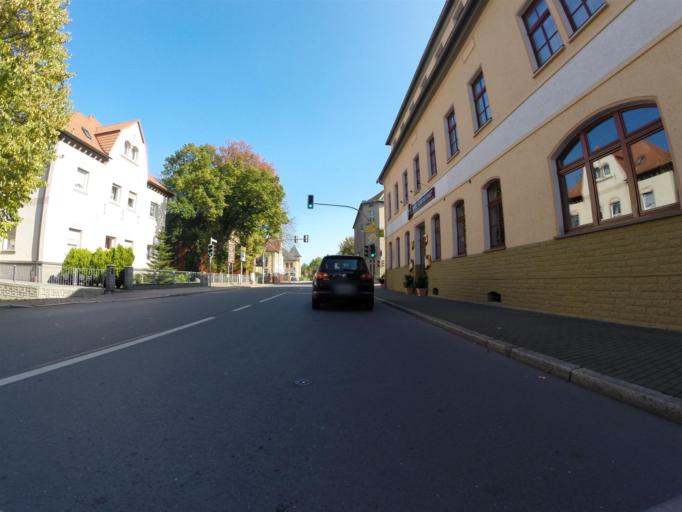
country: DE
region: Thuringia
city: Neustadt (Orla)
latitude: 50.7355
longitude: 11.7537
